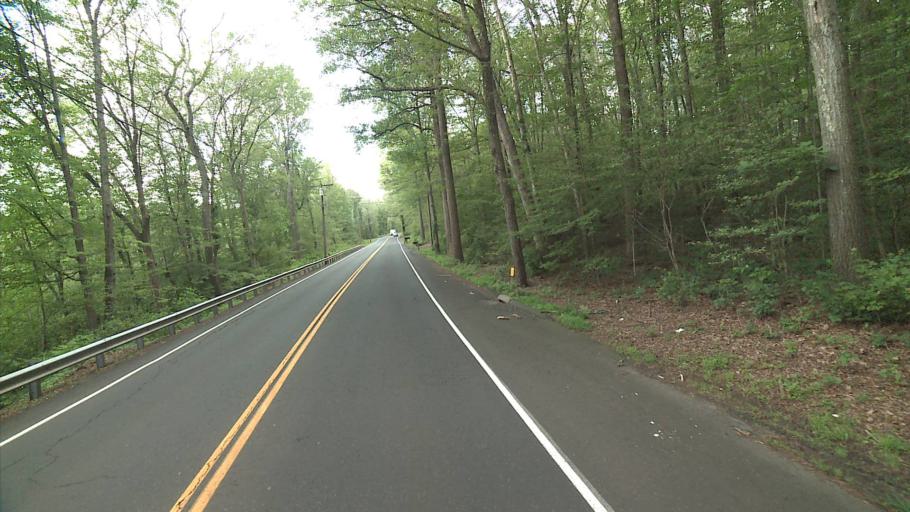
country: US
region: Connecticut
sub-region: Middlesex County
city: Higganum
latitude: 41.4087
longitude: -72.5616
